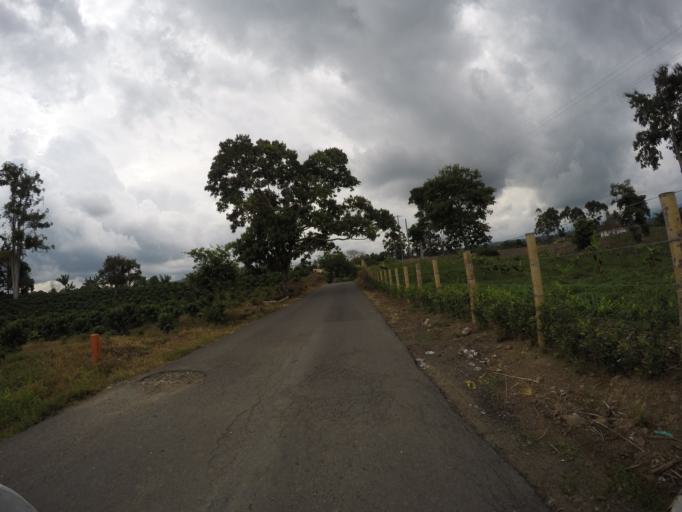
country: CO
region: Quindio
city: Quimbaya
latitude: 4.6105
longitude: -75.7161
